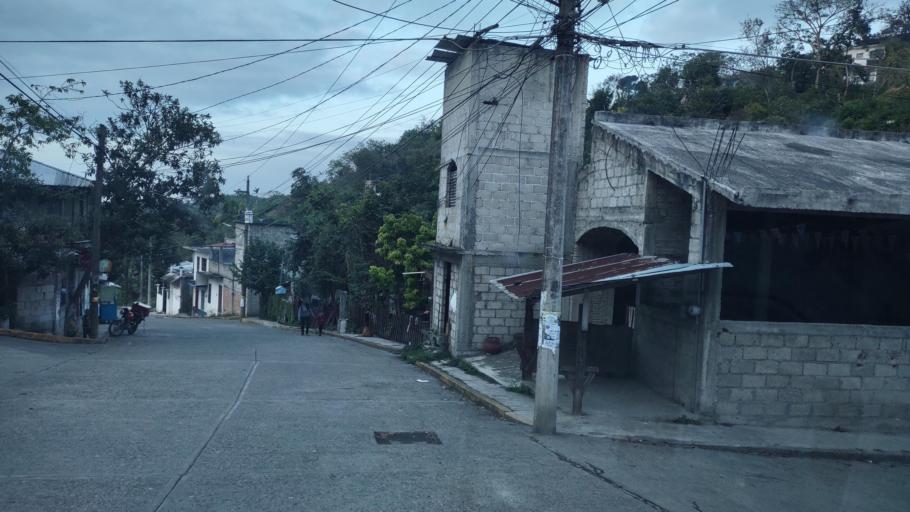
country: MX
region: Veracruz
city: Papantla de Olarte
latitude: 20.4564
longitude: -97.3065
